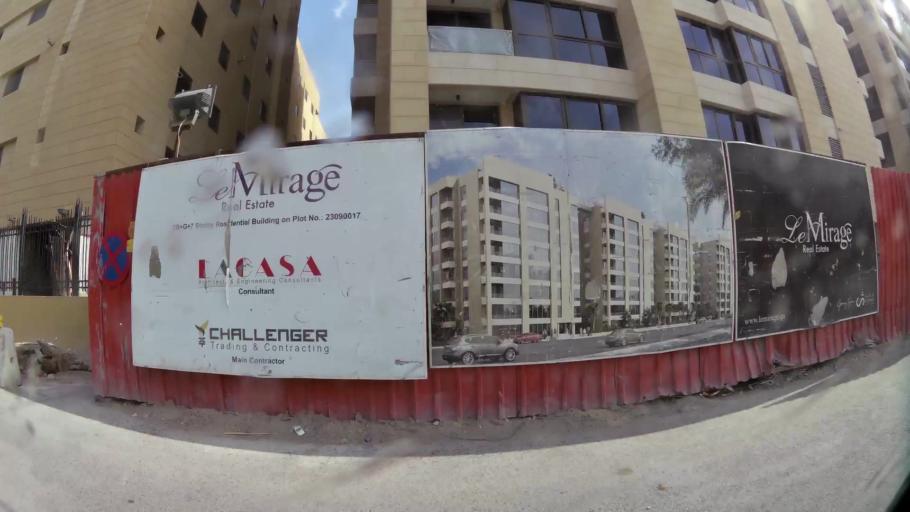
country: QA
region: Baladiyat ad Dawhah
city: Doha
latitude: 25.2788
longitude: 51.5151
